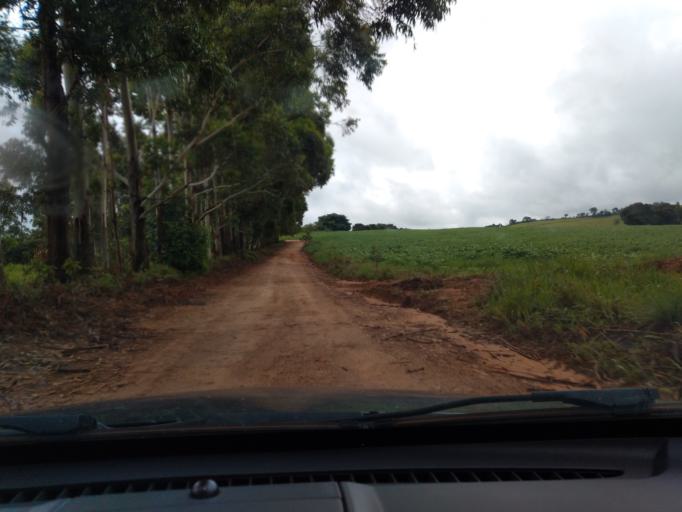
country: BR
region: Minas Gerais
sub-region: Lavras
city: Lavras
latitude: -21.5086
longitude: -44.9226
